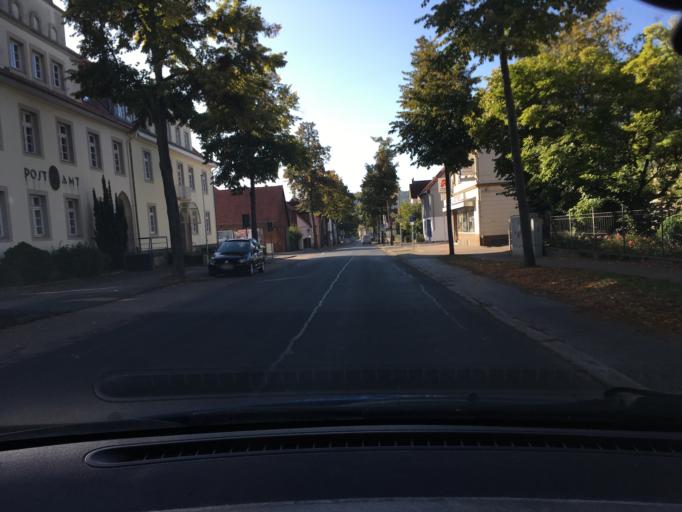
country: DE
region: Lower Saxony
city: Springe
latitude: 52.2129
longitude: 9.5574
